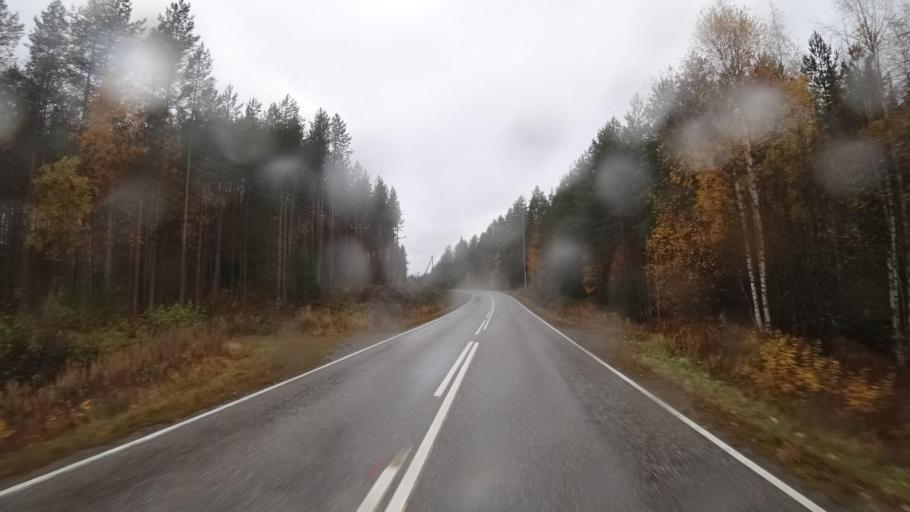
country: FI
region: North Karelia
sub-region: Joensuu
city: Outokumpu
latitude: 62.6204
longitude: 28.9253
